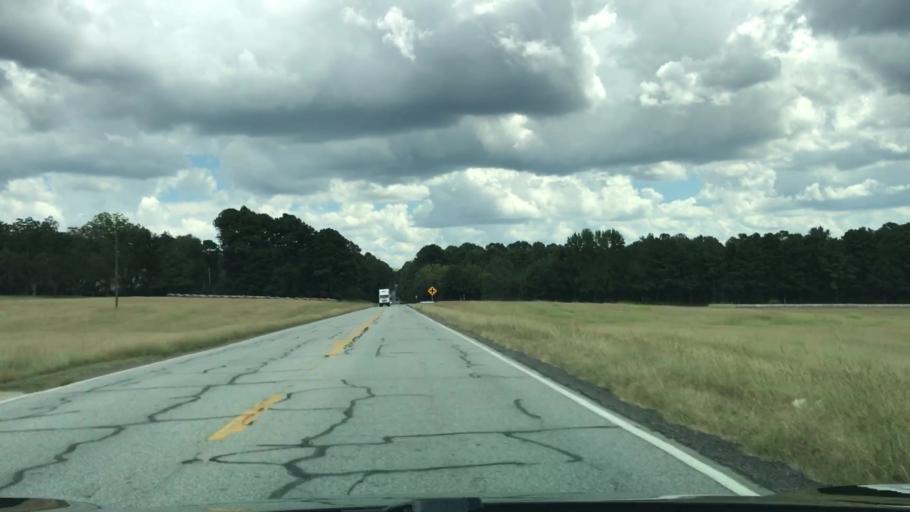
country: US
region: Georgia
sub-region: Barrow County
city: Russell
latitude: 33.9605
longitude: -83.6665
